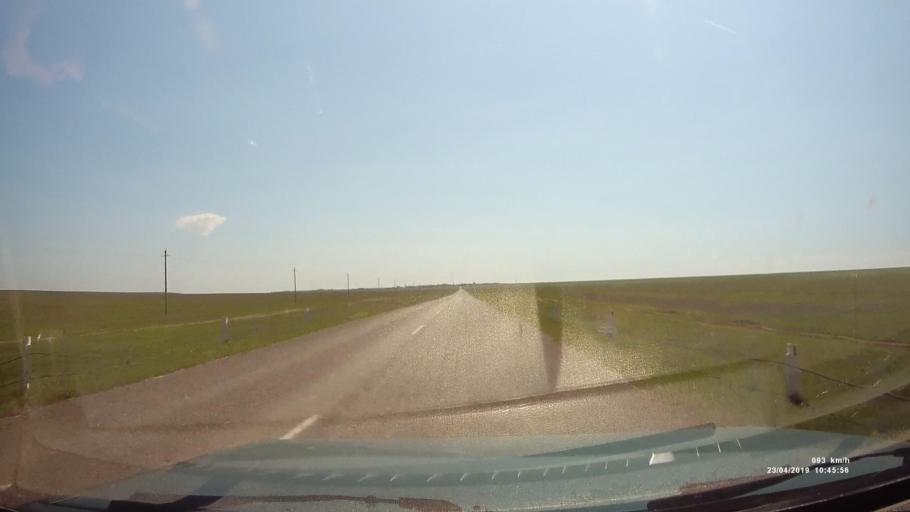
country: RU
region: Kalmykiya
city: Yashalta
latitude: 46.4471
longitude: 42.6829
